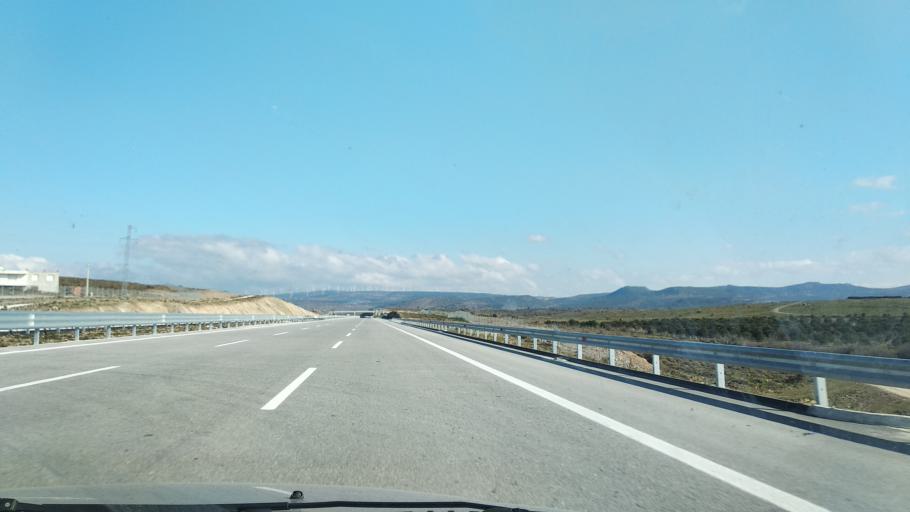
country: TR
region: Izmir
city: Yenisakran
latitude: 38.8553
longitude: 27.0614
